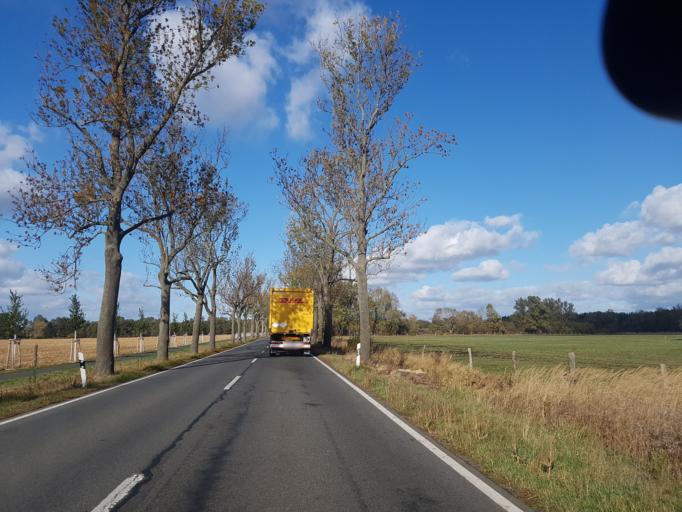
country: DE
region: Brandenburg
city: Nauen
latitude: 52.6518
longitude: 12.9249
